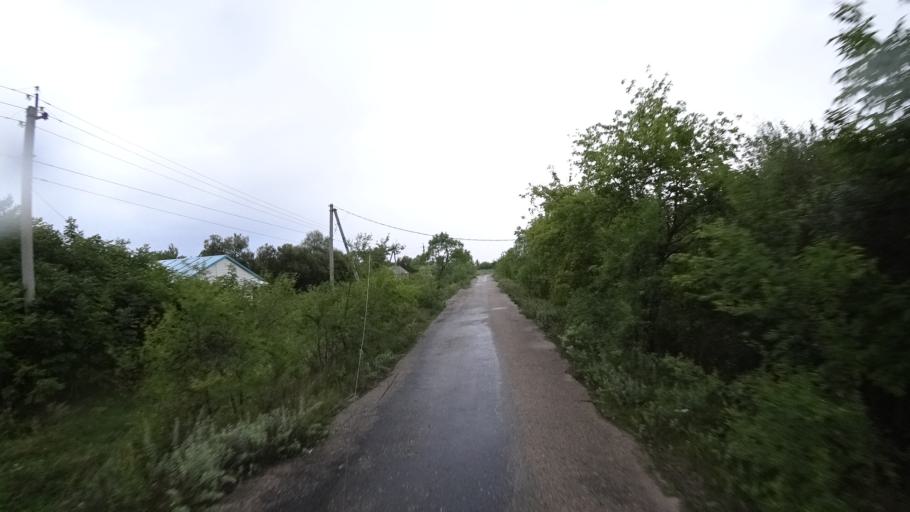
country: RU
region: Primorskiy
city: Chernigovka
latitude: 44.4037
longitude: 132.5316
